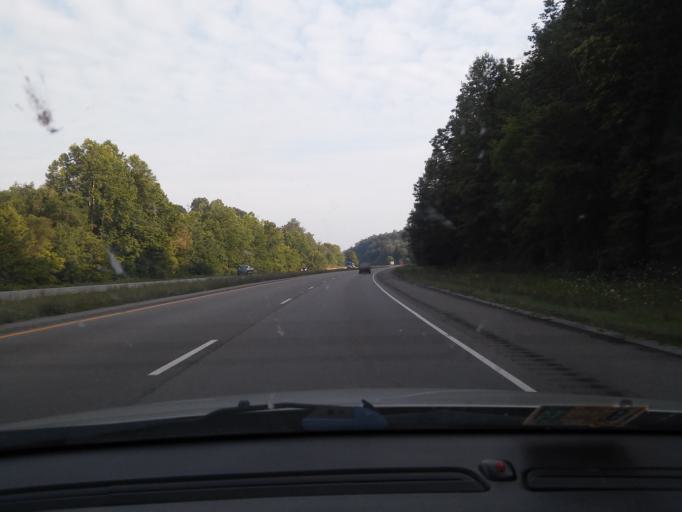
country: US
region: Ohio
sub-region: Jackson County
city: Oak Hill
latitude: 38.9181
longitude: -82.4607
